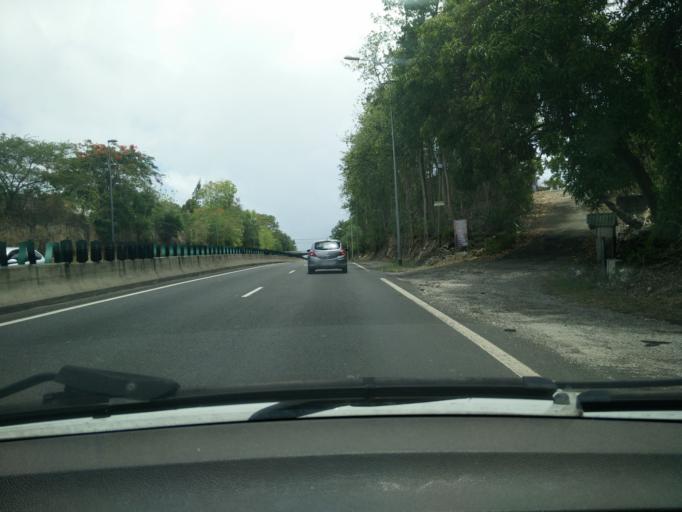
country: GP
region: Guadeloupe
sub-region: Guadeloupe
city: Pointe-a-Pitre
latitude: 16.2313
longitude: -61.5240
